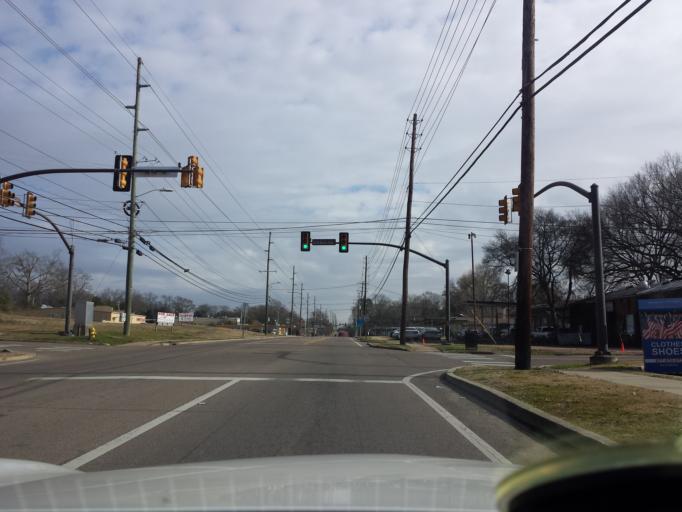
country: US
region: Mississippi
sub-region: Oktibbeha County
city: Starkville
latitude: 33.4659
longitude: -88.8168
